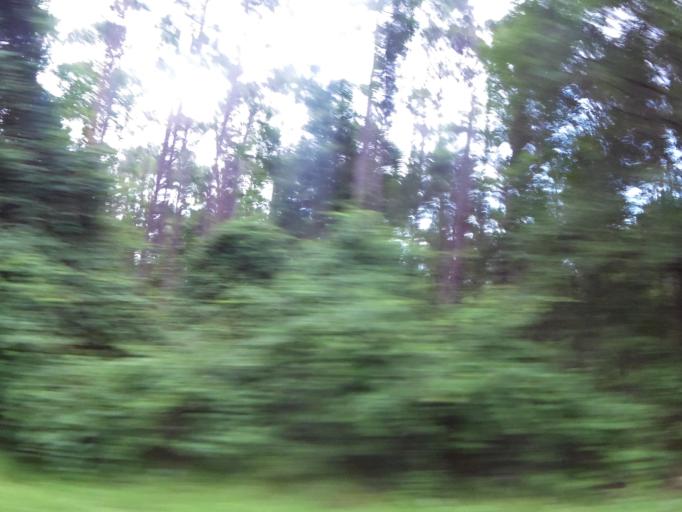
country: US
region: Florida
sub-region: Duval County
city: Jacksonville
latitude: 30.3452
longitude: -81.7856
